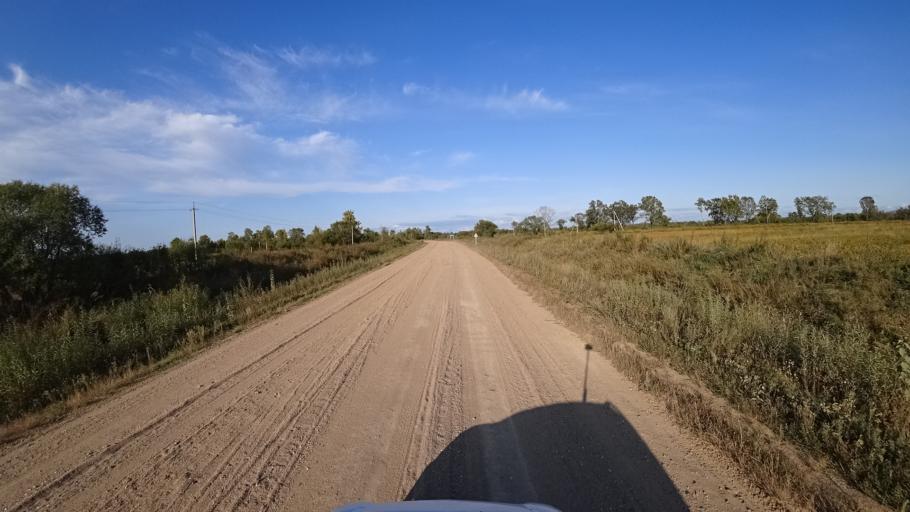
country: RU
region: Amur
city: Arkhara
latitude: 49.3524
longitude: 130.1338
